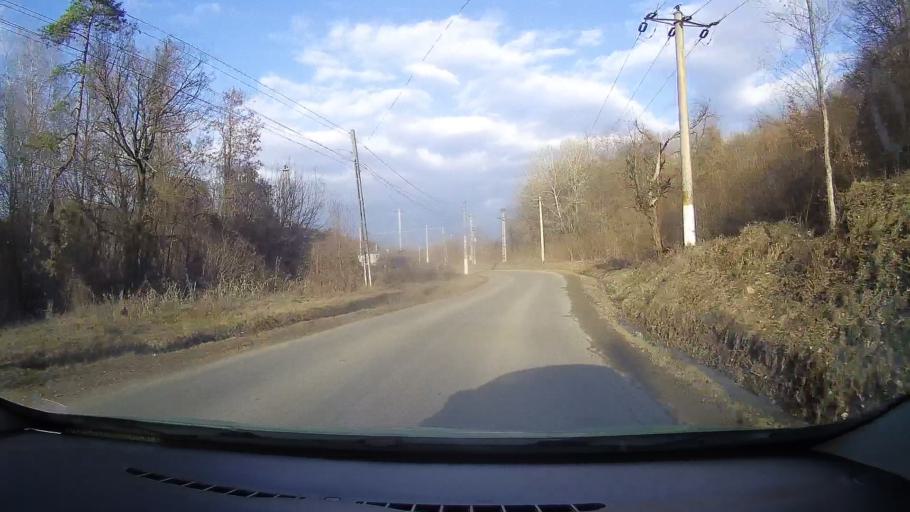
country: RO
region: Dambovita
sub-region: Comuna Ocnita
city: Ocnita
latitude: 44.9694
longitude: 25.5479
